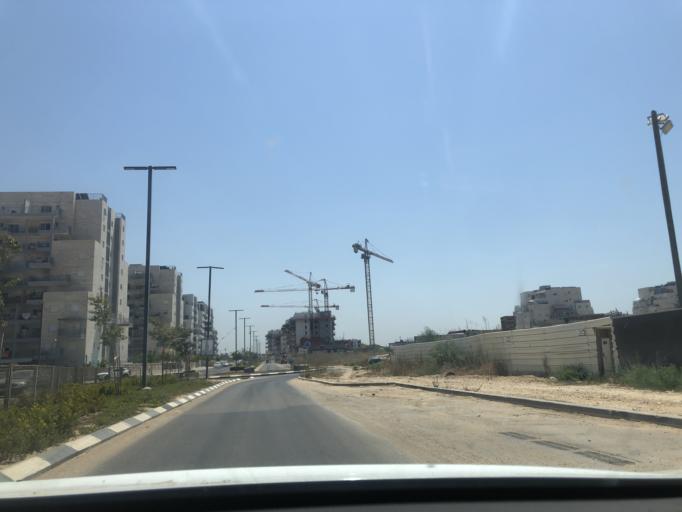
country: IL
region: Central District
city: Lod
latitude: 31.9386
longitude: 34.8986
